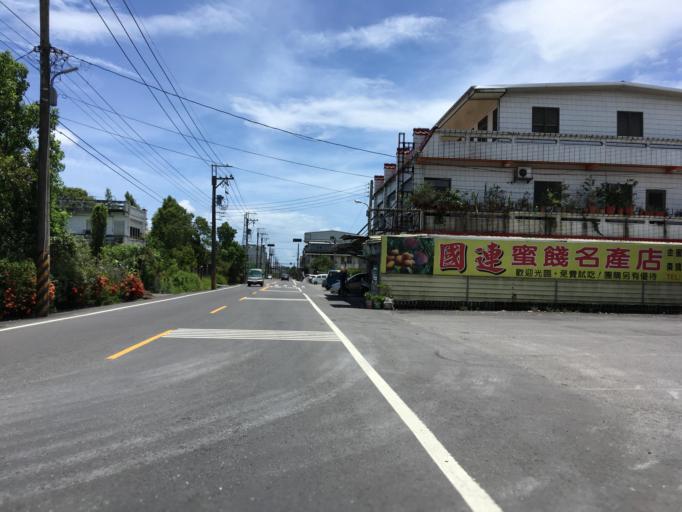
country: TW
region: Taiwan
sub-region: Yilan
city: Yilan
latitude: 24.6651
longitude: 121.7417
